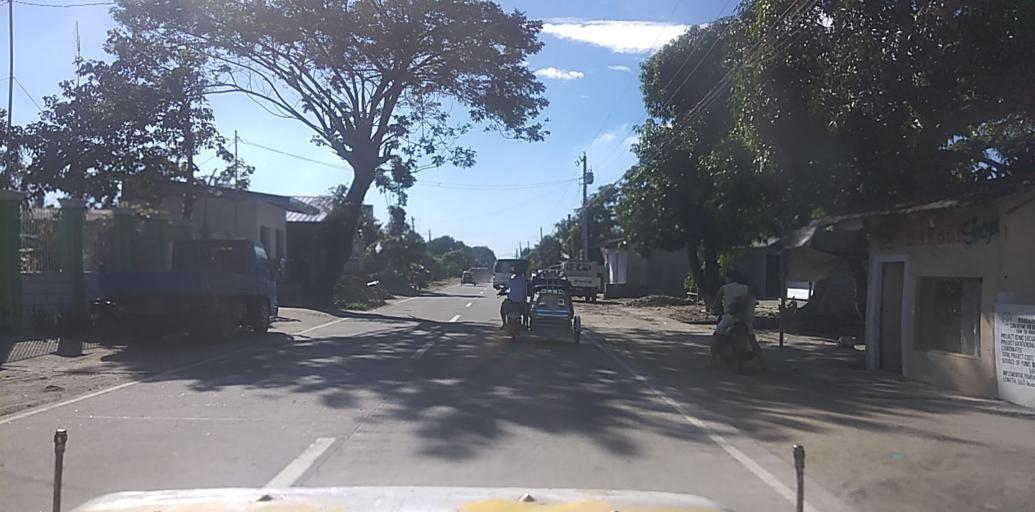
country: PH
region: Central Luzon
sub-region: Province of Pampanga
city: Mexico
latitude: 15.0829
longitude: 120.7161
